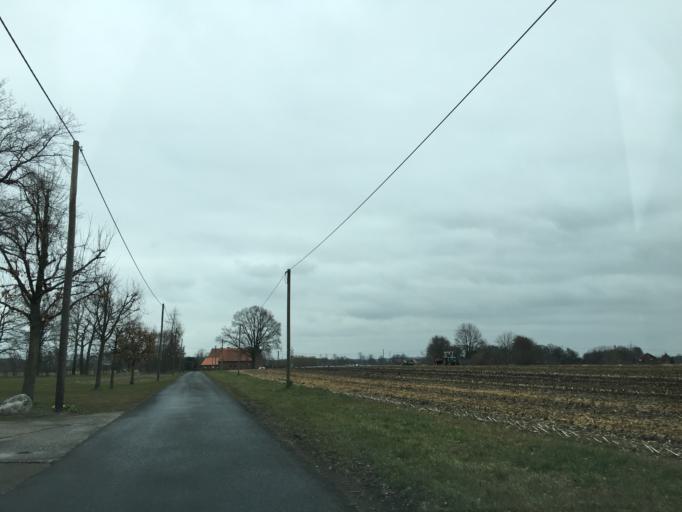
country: DE
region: North Rhine-Westphalia
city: Ludinghausen
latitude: 51.7628
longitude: 7.4746
